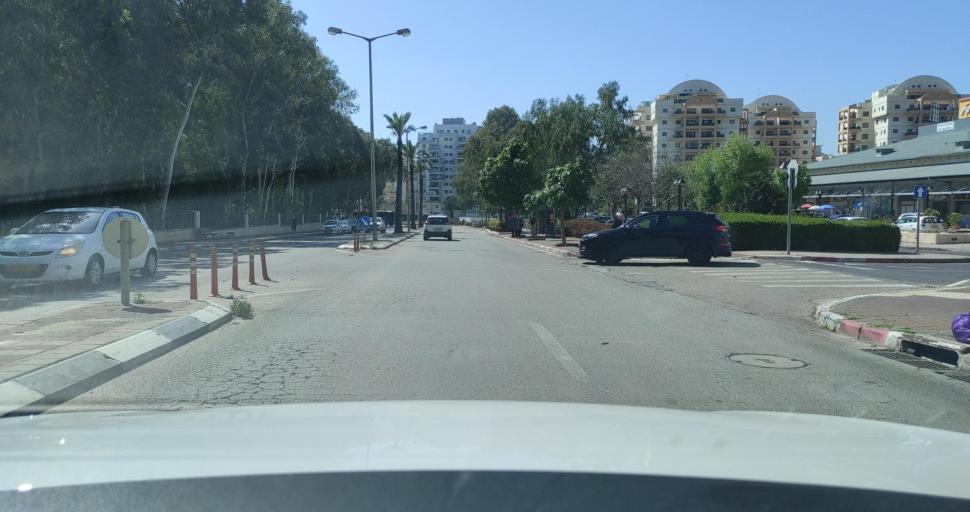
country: IL
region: Central District
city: Nordiyya
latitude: 32.3069
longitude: 34.8764
